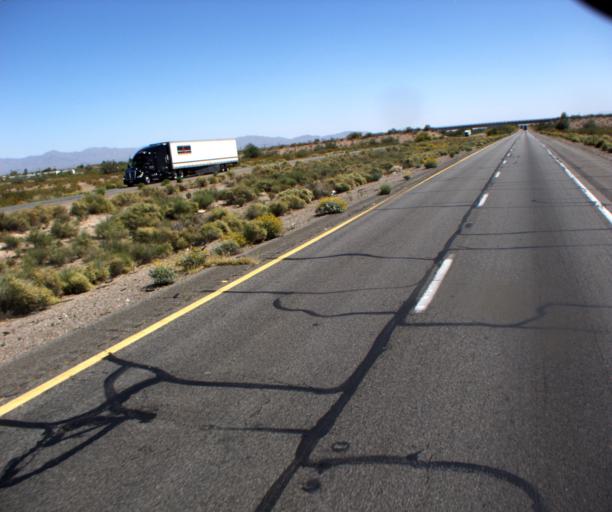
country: US
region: Arizona
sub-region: Maricopa County
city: Buckeye
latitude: 33.4711
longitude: -112.8201
